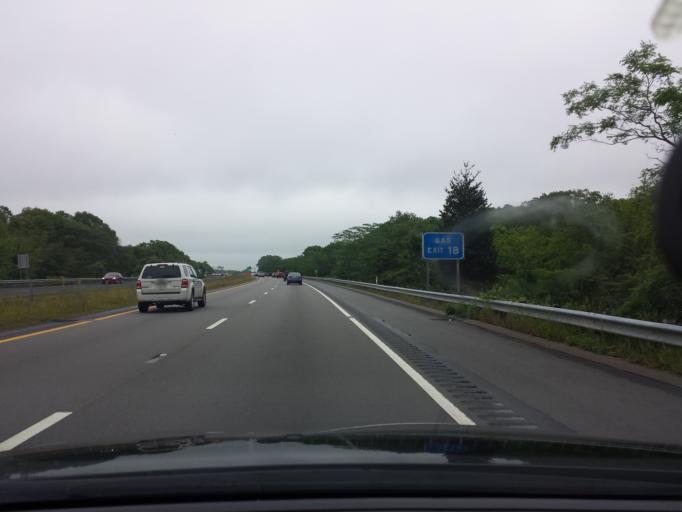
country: US
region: Massachusetts
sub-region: Bristol County
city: Fairhaven
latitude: 41.6548
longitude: -70.9011
